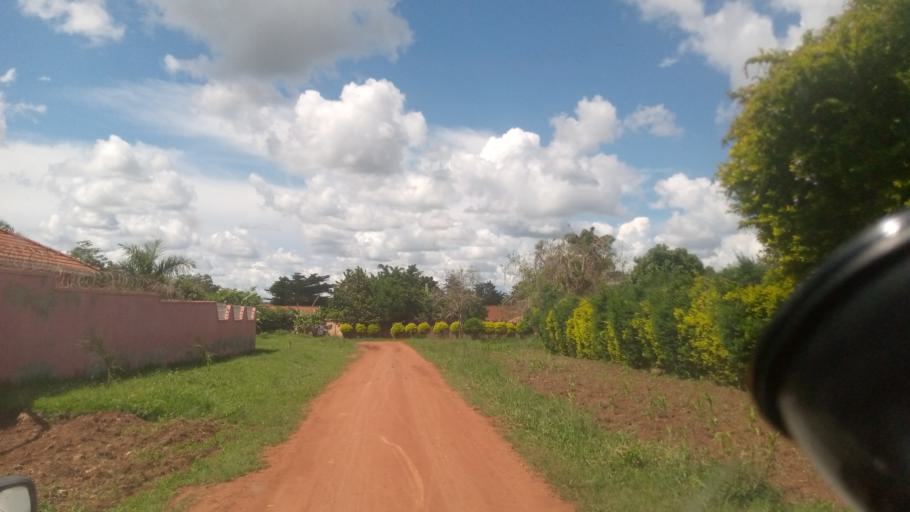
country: UG
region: Northern Region
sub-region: Lira District
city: Lira
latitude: 2.2371
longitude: 32.9056
